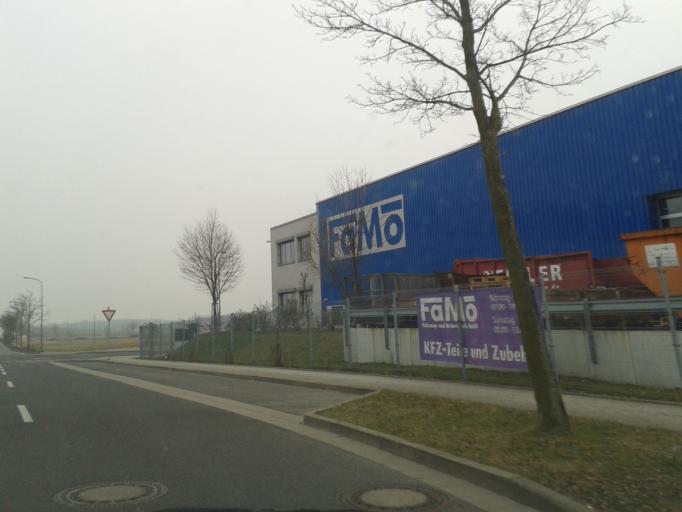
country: DE
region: Saxony
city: Bannewitz
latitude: 51.0117
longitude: 13.7016
